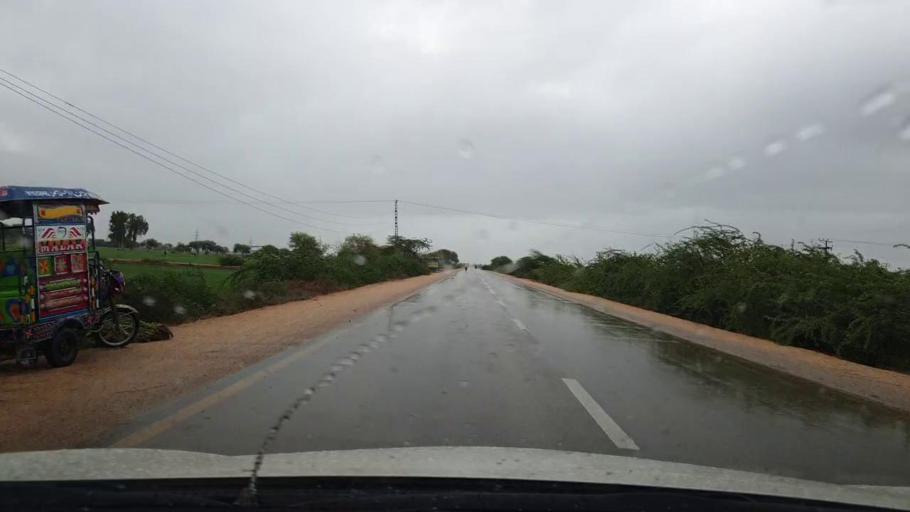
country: PK
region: Sindh
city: Kario
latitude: 24.6533
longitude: 68.5789
